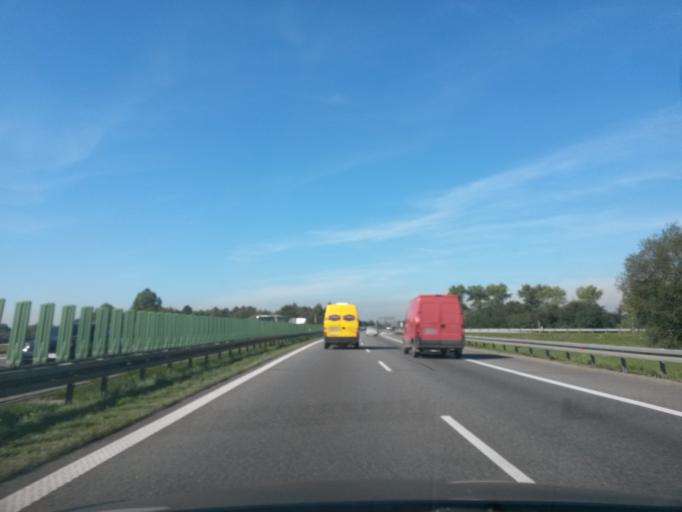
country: PL
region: Lesser Poland Voivodeship
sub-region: Powiat krakowski
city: Piekary
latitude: 50.0204
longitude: 19.8298
